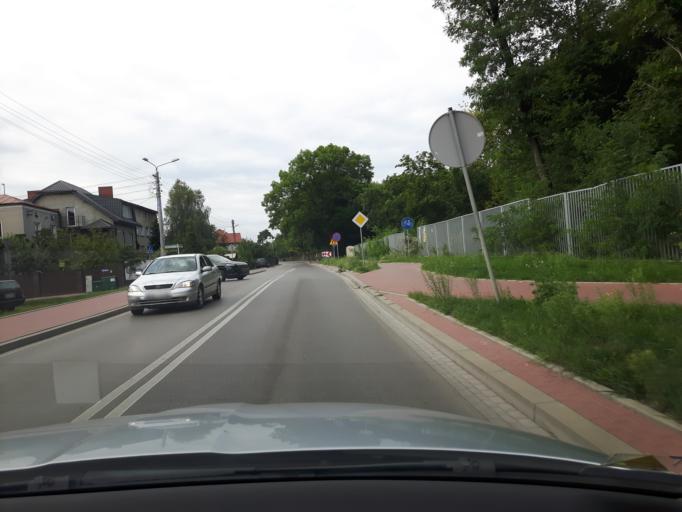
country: PL
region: Masovian Voivodeship
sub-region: Powiat wolominski
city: Zabki
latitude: 52.3035
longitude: 21.1063
